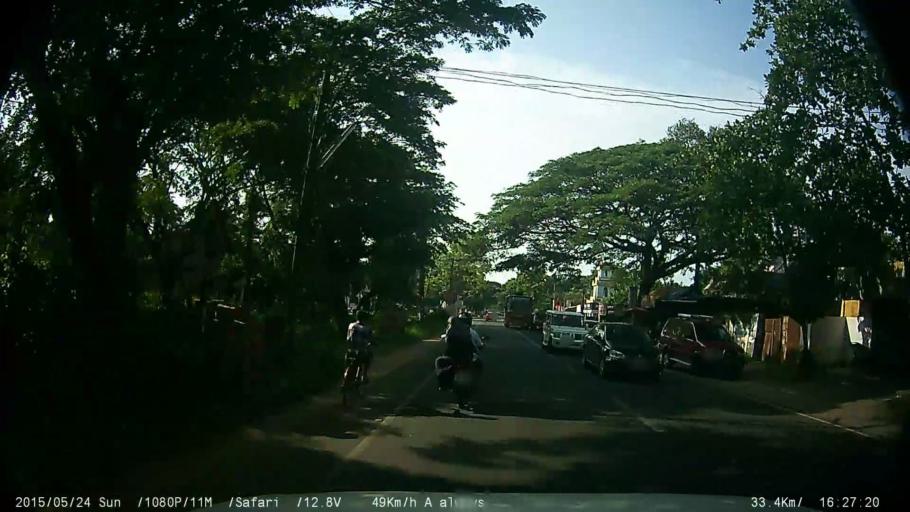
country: IN
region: Kerala
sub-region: Alappuzha
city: Alleppey
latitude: 9.5279
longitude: 76.3275
